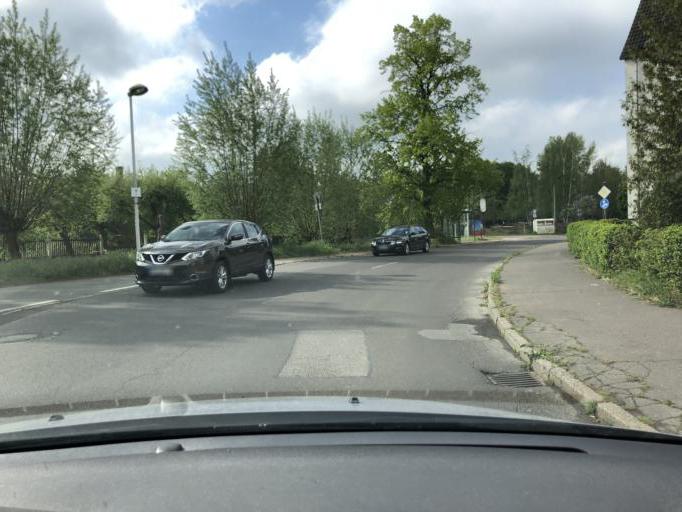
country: DE
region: Thuringia
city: Altenburg
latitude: 51.0067
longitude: 12.4418
